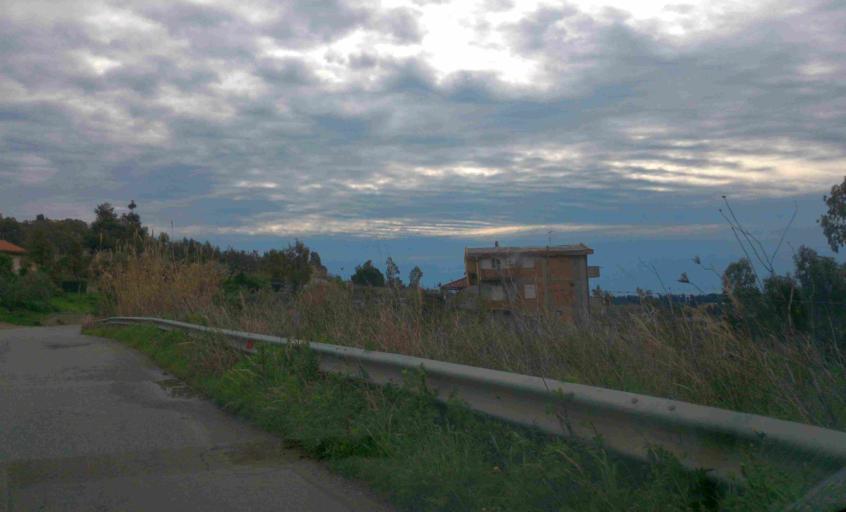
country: IT
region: Calabria
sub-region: Provincia di Catanzaro
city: Sellia Marina
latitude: 38.8891
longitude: 16.7079
